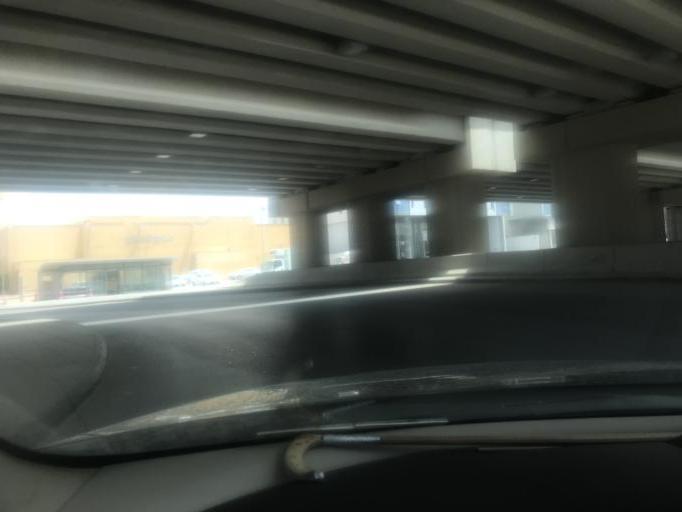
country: SA
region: Ar Riyad
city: Riyadh
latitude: 24.7900
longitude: 46.7017
